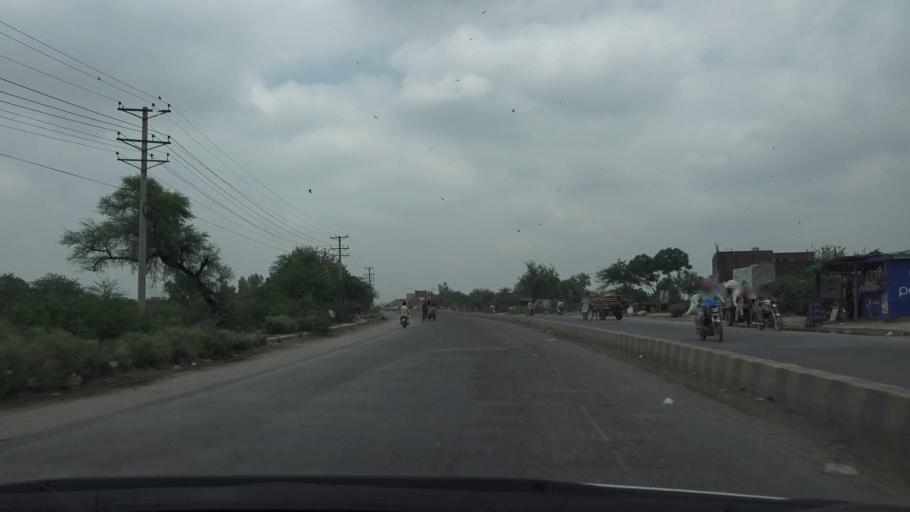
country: PK
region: Punjab
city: Faisalabad
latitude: 31.3906
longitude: 73.1898
